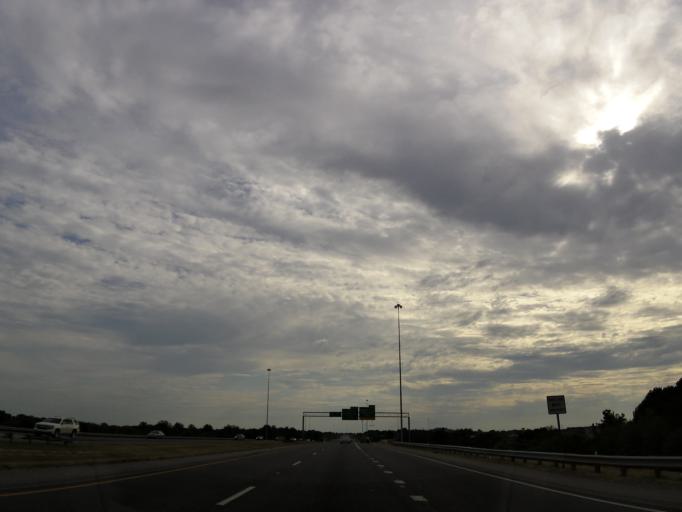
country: US
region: Alabama
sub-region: Madison County
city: Madison
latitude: 34.6774
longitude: -86.7431
